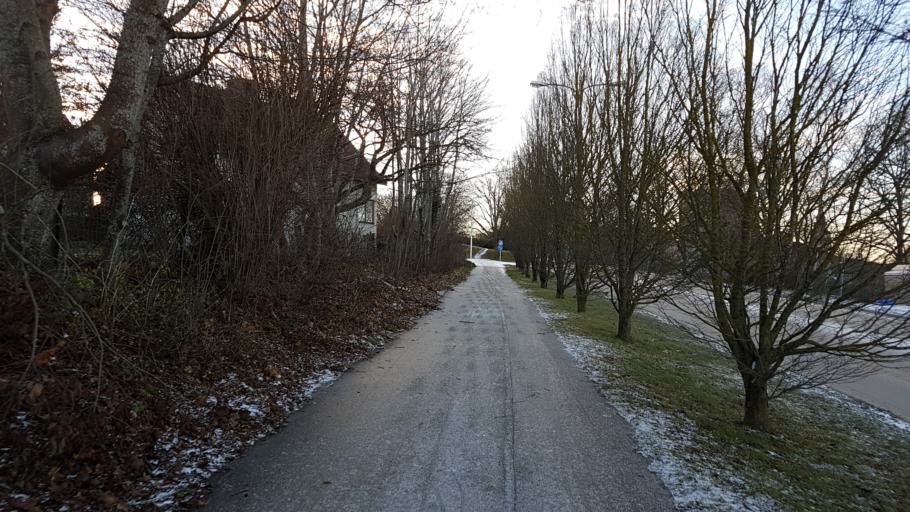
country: SE
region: Gotland
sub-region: Gotland
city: Visby
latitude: 57.6460
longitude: 18.3020
